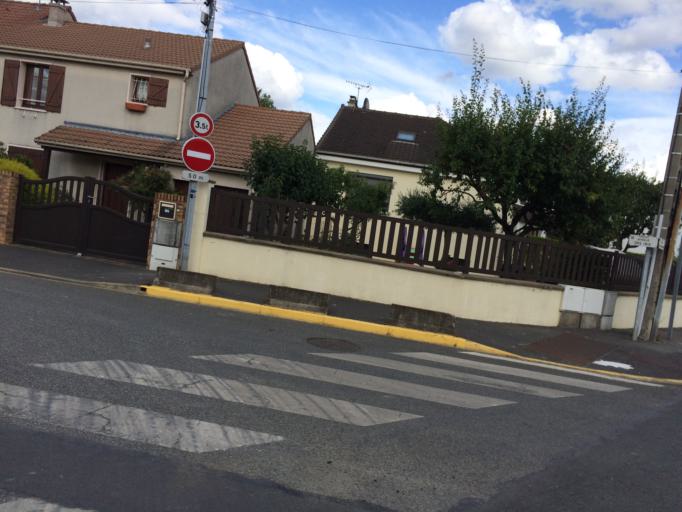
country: FR
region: Ile-de-France
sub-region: Departement de l'Essonne
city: Morangis
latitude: 48.7037
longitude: 2.3435
